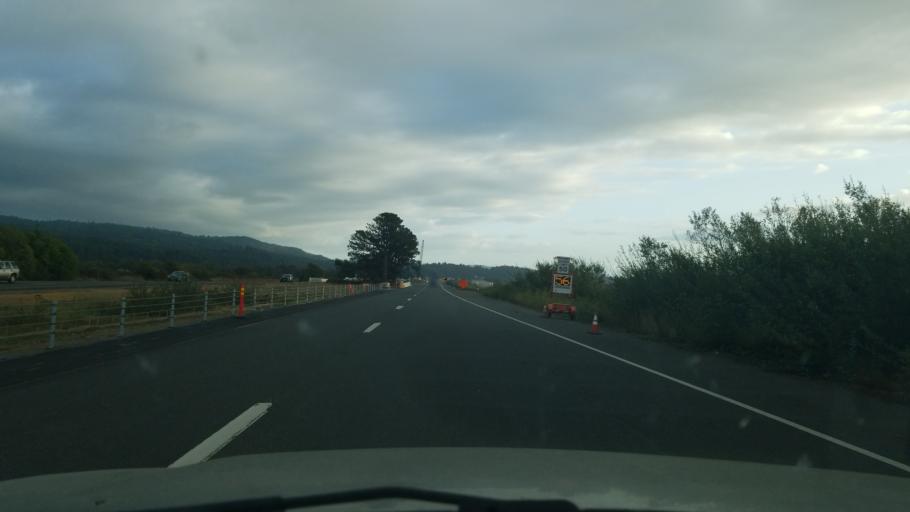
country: US
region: California
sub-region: Humboldt County
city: Arcata
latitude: 40.8488
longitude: -124.0821
